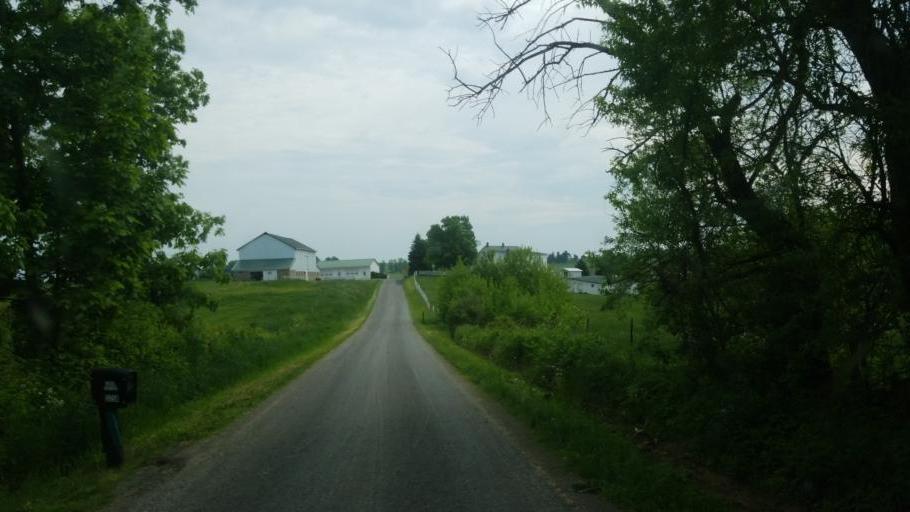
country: US
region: Ohio
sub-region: Wayne County
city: Apple Creek
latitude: 40.6808
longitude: -81.7382
